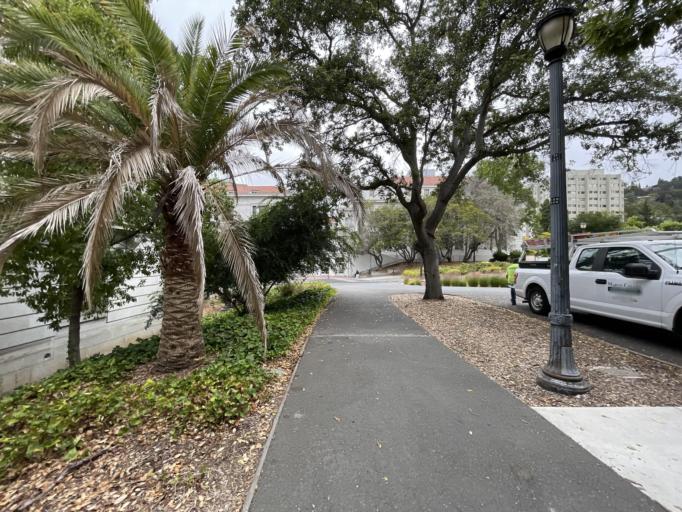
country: US
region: California
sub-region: Alameda County
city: Berkeley
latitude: 37.8716
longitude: -122.2588
